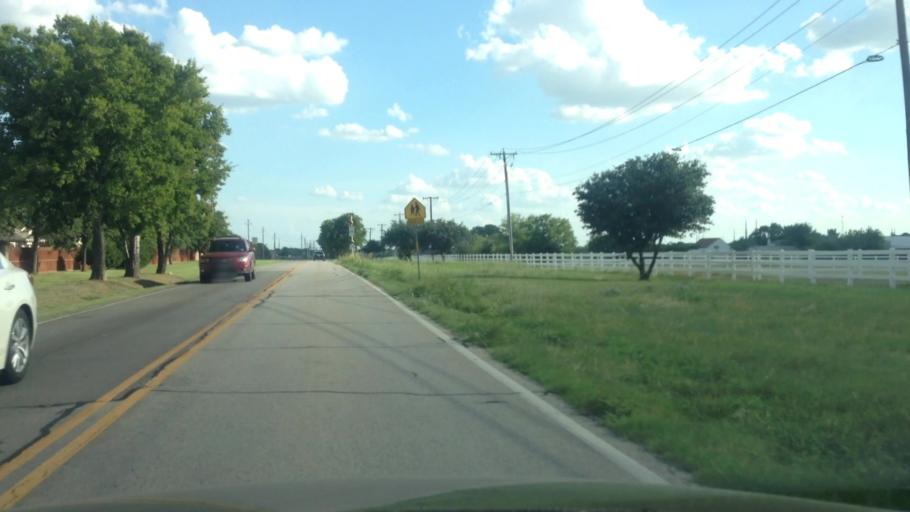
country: US
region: Texas
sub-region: Tarrant County
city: Saginaw
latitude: 32.9195
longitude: -97.3750
